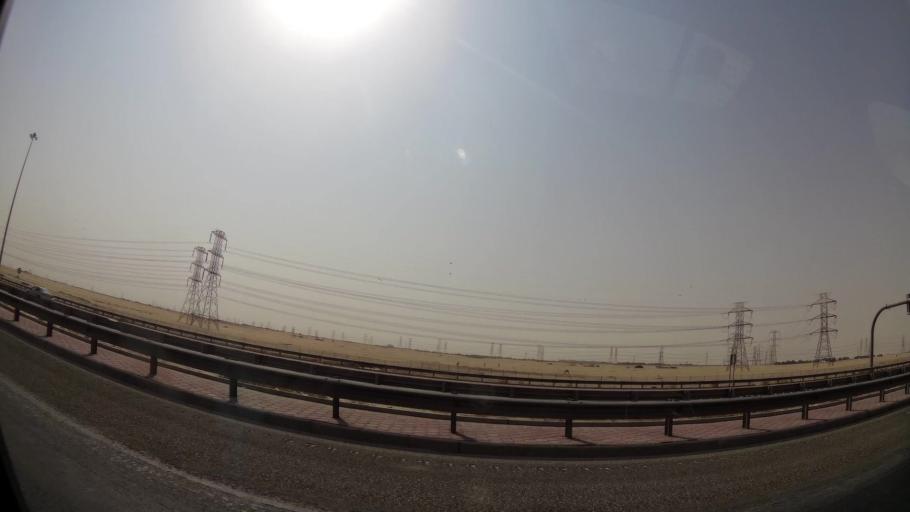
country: KW
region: Muhafazat al Jahra'
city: Al Jahra'
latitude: 29.2989
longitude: 47.7081
